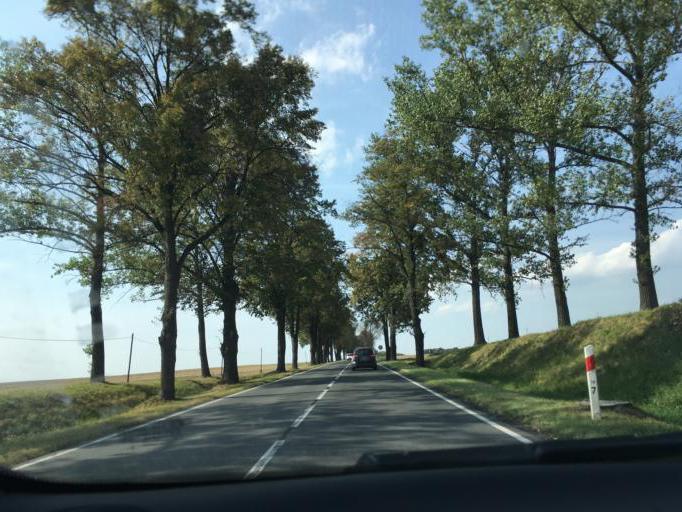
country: PL
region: Opole Voivodeship
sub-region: Powiat prudnicki
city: Laka Prudnicka
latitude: 50.3888
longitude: 17.5185
